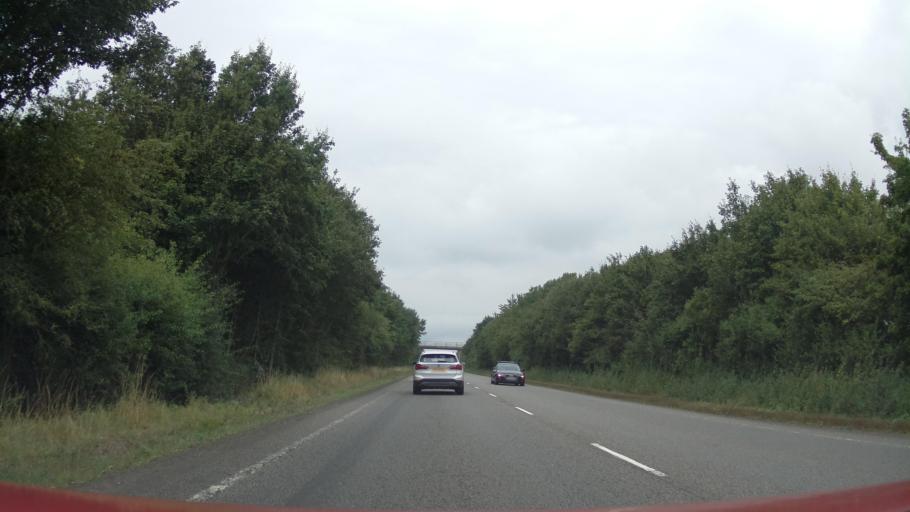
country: GB
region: England
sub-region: Nottinghamshire
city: South Collingham
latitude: 53.0916
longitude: -0.7666
